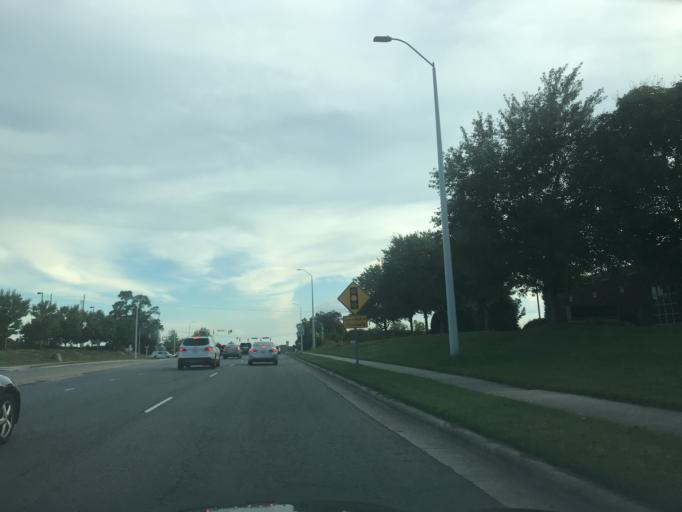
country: US
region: North Carolina
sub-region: Wake County
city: Green Level
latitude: 35.7896
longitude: -78.8707
